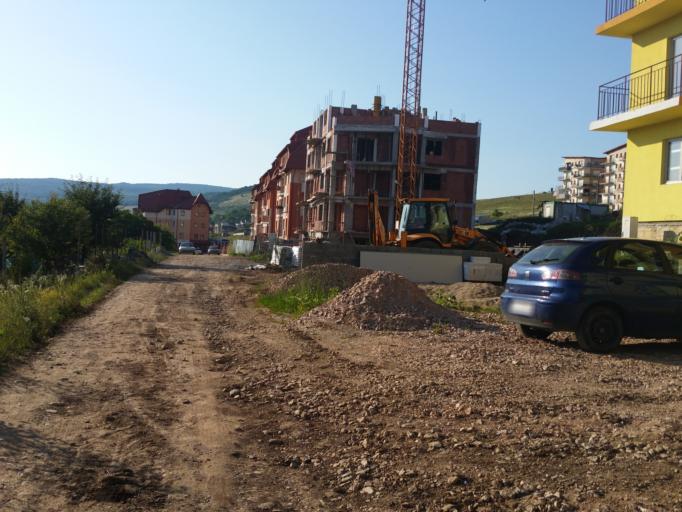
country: RO
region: Cluj
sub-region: Comuna Baciu
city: Baciu
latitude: 46.7899
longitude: 23.5316
